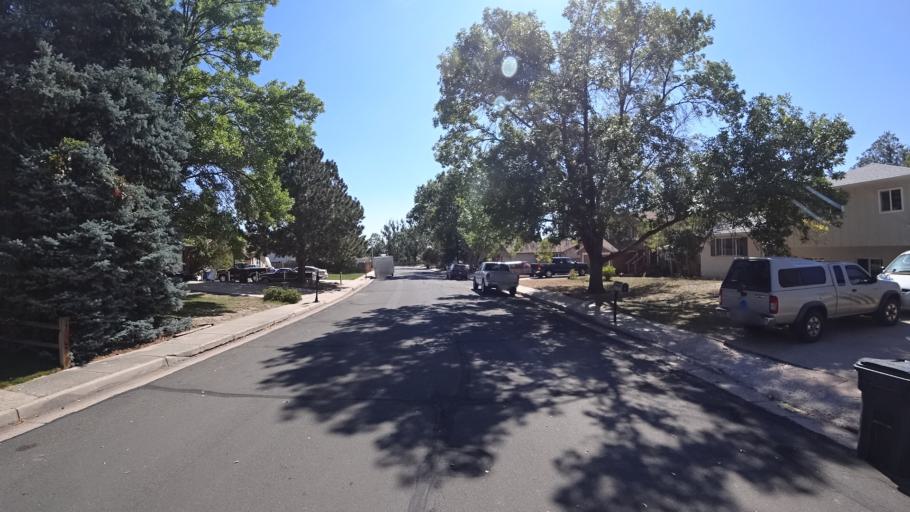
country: US
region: Colorado
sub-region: El Paso County
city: Cimarron Hills
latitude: 38.9021
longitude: -104.7608
